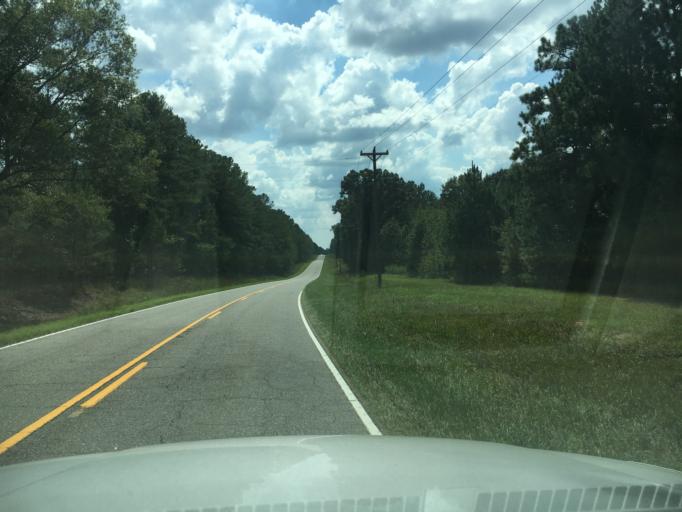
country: US
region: South Carolina
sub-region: Greenwood County
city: Greenwood
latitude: 34.0989
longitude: -82.1288
